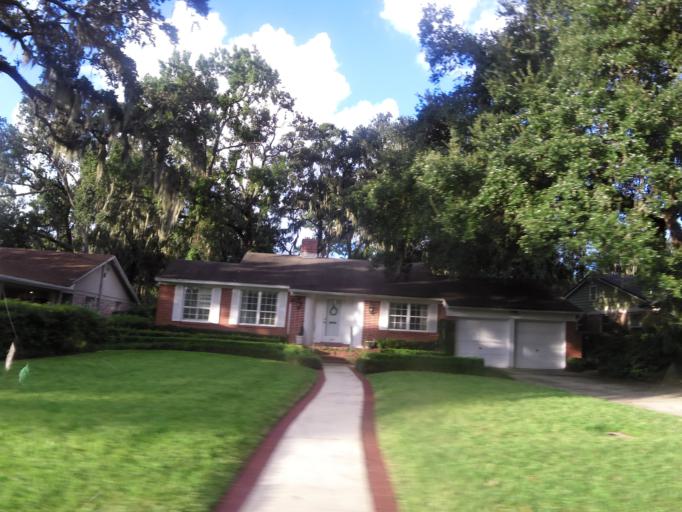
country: US
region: Florida
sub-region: Duval County
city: Jacksonville
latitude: 30.2886
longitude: -81.6535
